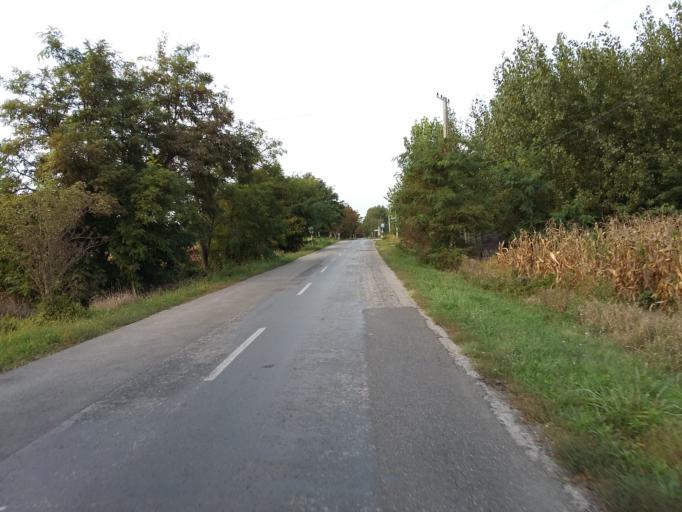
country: HU
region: Csongrad
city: Szeged
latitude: 46.2170
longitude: 20.1102
